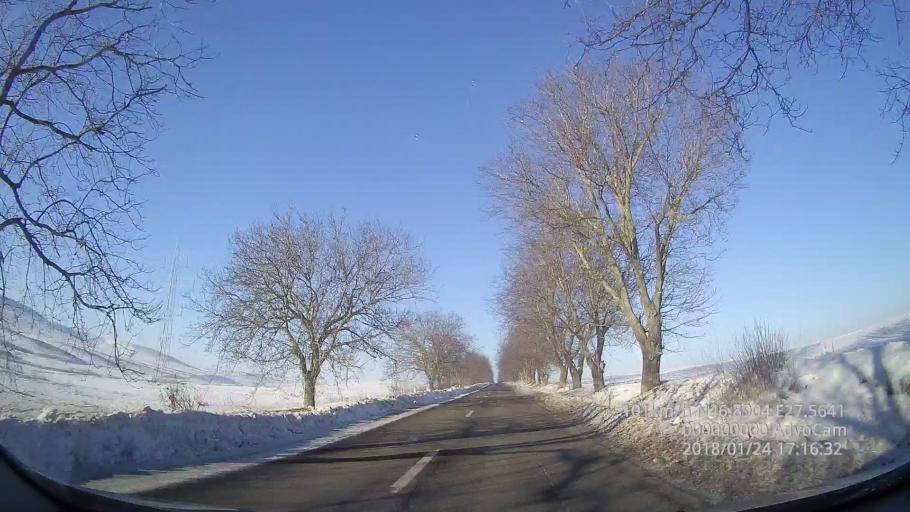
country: RO
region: Iasi
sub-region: Comuna Scanteia
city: Scanteia
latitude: 46.8912
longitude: 27.5641
